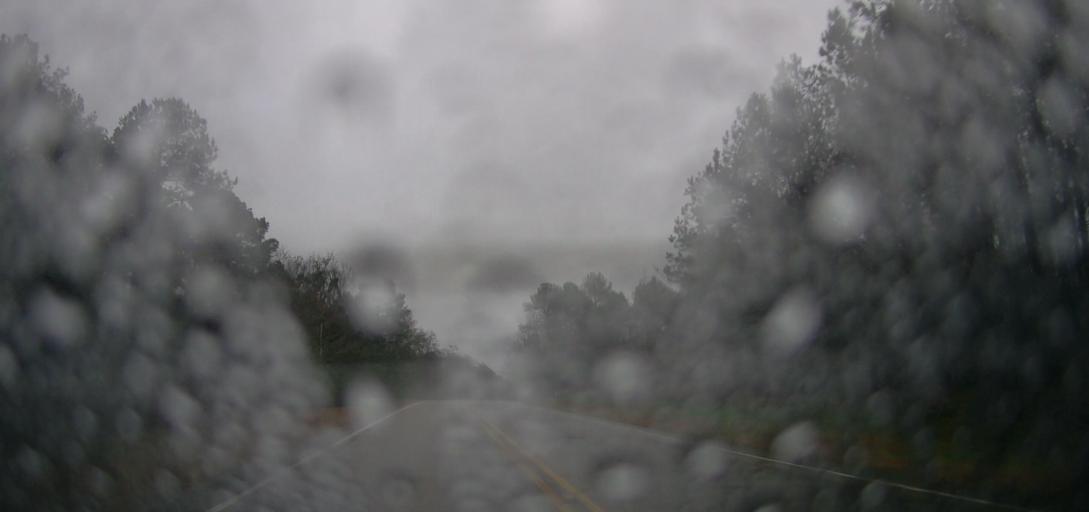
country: US
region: Alabama
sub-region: Autauga County
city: Pine Level
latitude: 32.5202
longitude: -86.6071
